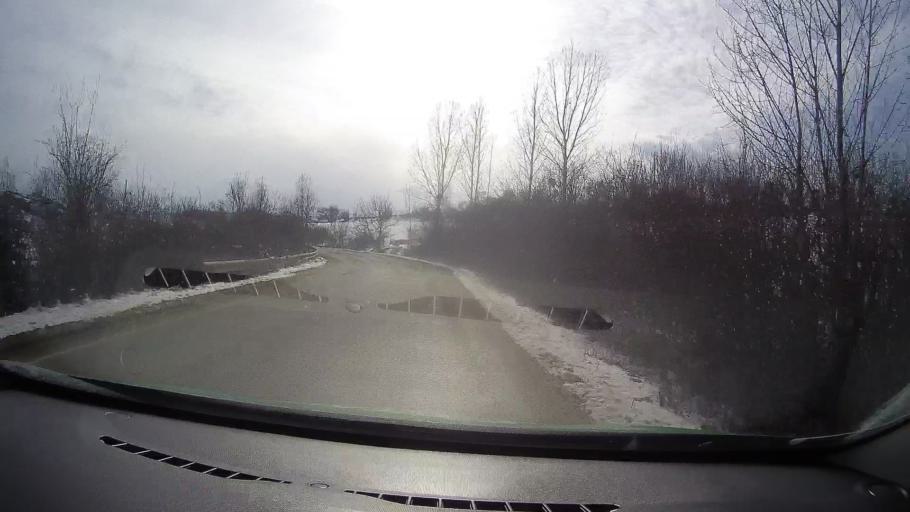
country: RO
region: Sibiu
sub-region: Comuna Bradeni
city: Bradeni
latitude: 46.1054
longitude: 24.8414
